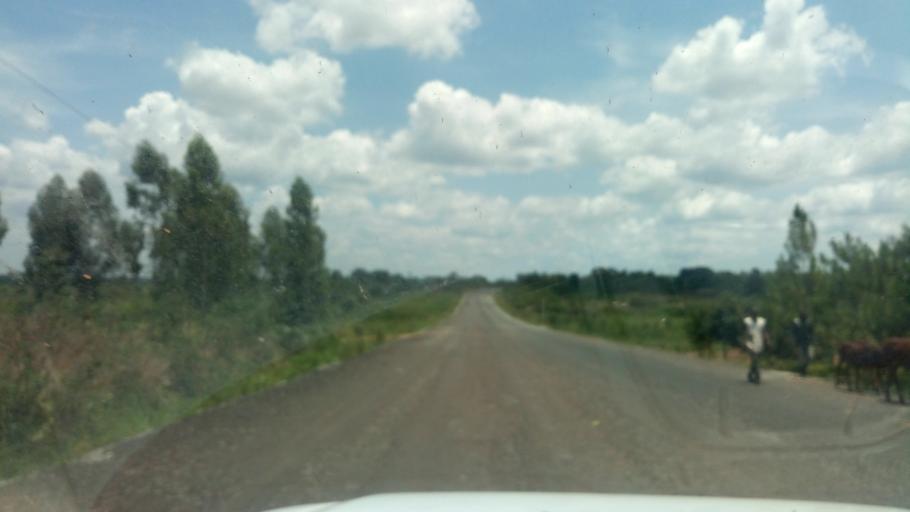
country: UG
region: Western Region
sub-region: Kiryandongo District
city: Kiryandongo
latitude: 1.7902
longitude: 31.9391
